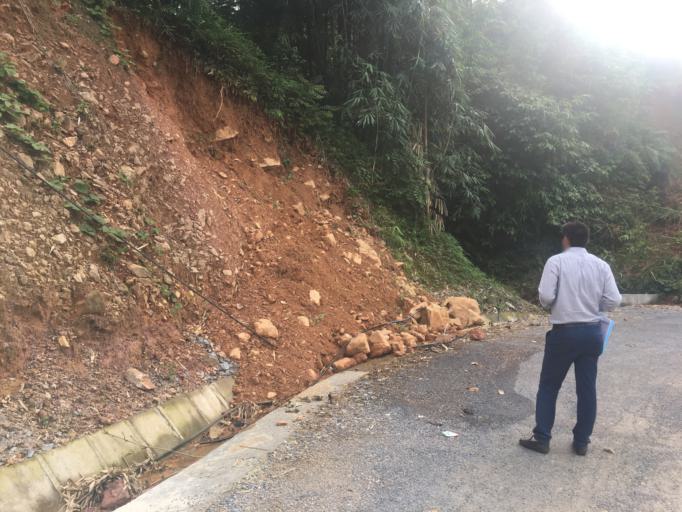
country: VN
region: Ha Giang
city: Thanh Pho Ha Giang
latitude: 22.9018
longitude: 105.0213
